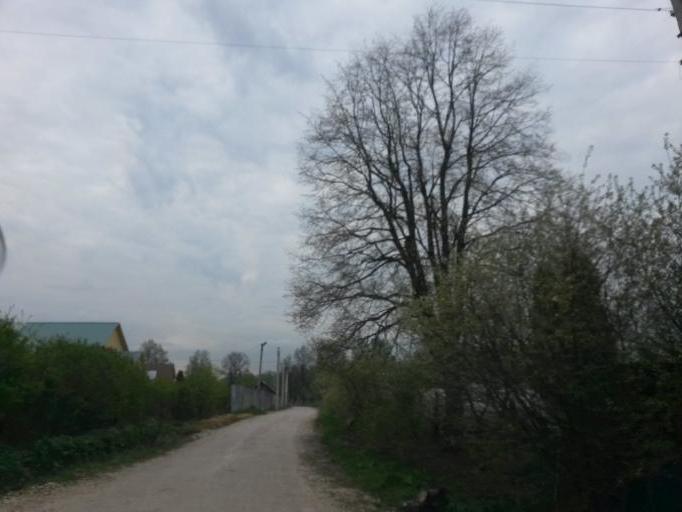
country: RU
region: Moskovskaya
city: Lyubuchany
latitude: 55.2528
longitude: 37.6079
